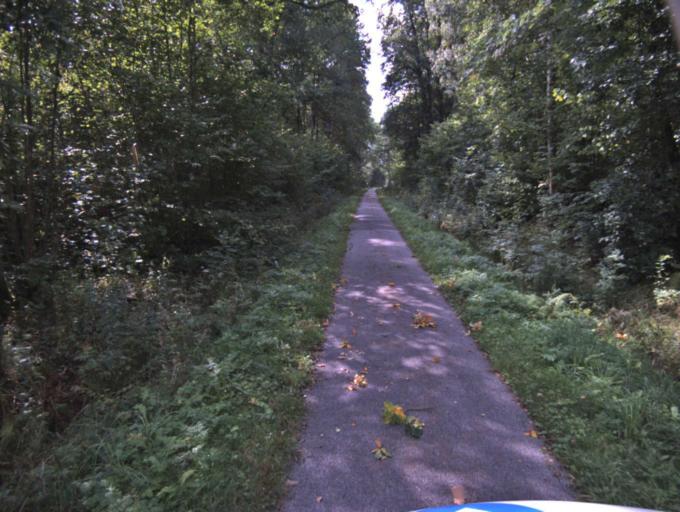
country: SE
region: Vaestra Goetaland
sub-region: Tranemo Kommun
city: Limmared
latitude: 57.6342
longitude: 13.3531
